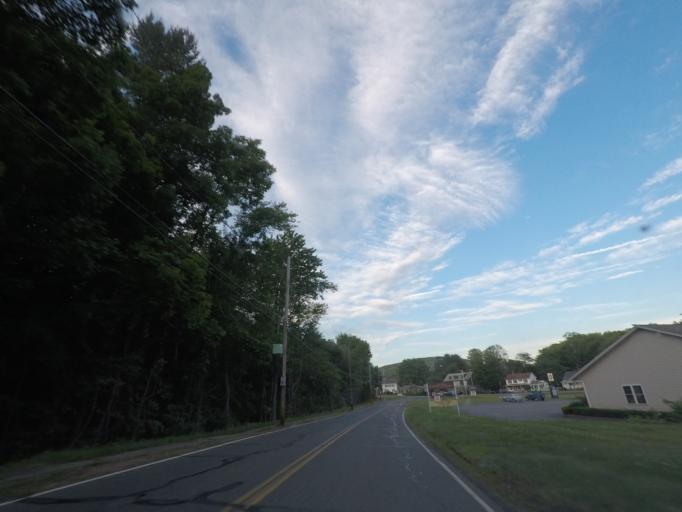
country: US
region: Massachusetts
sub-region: Hampshire County
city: Ware
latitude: 42.2121
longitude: -72.2438
